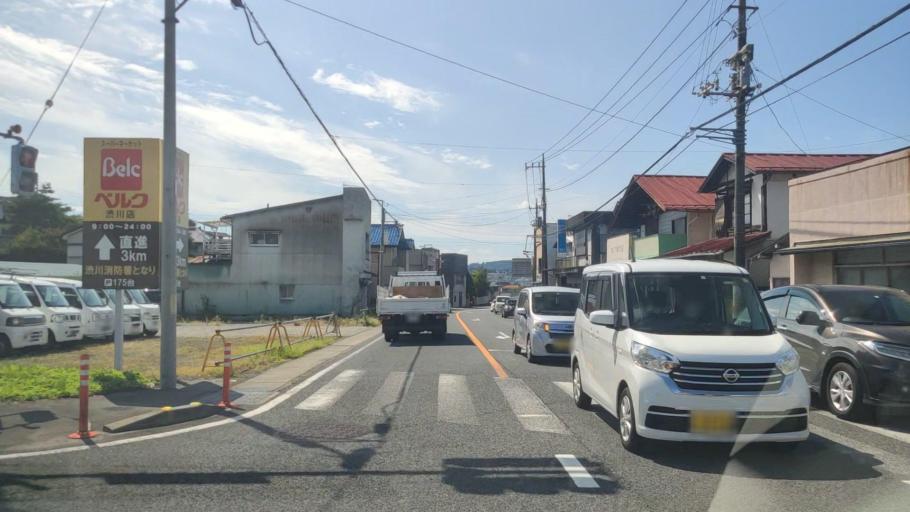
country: JP
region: Gunma
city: Shibukawa
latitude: 36.5165
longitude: 139.0074
